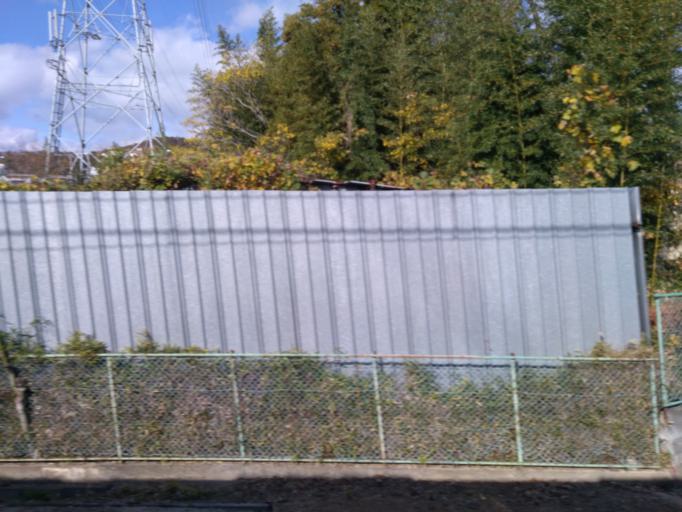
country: JP
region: Hyogo
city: Kawanishi
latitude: 34.8239
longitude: 135.3956
